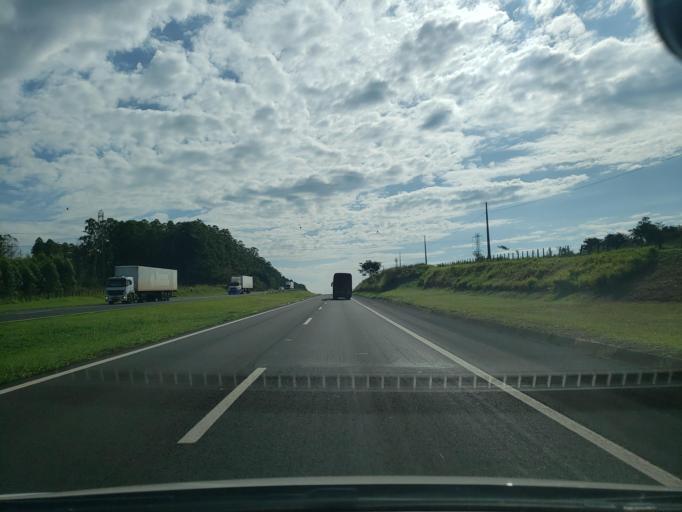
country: BR
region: Sao Paulo
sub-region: Lins
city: Lins
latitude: -21.6720
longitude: -49.7801
